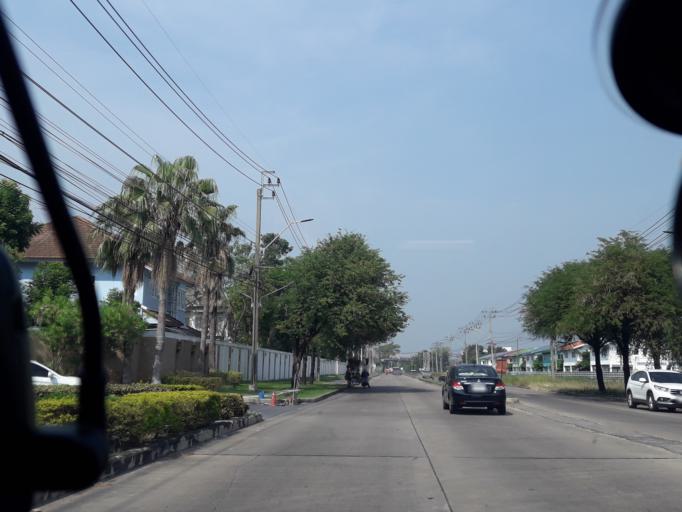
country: TH
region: Bangkok
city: Khlong Sam Wa
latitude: 13.8571
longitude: 100.7071
